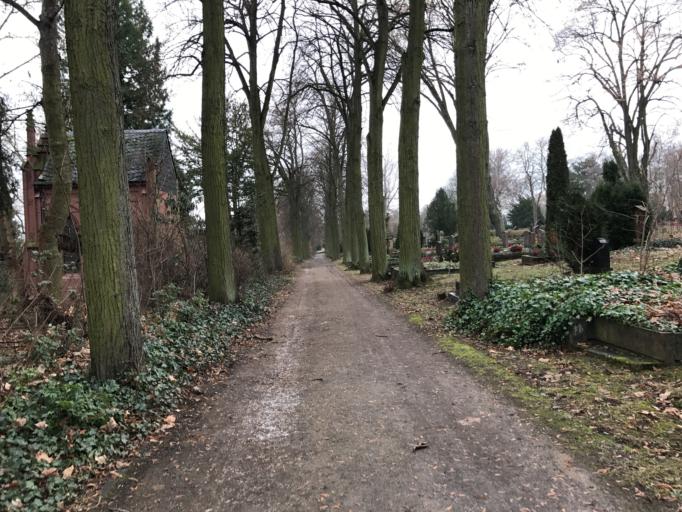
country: DE
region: Rheinland-Pfalz
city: Mainz
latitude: 49.9959
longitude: 8.2489
